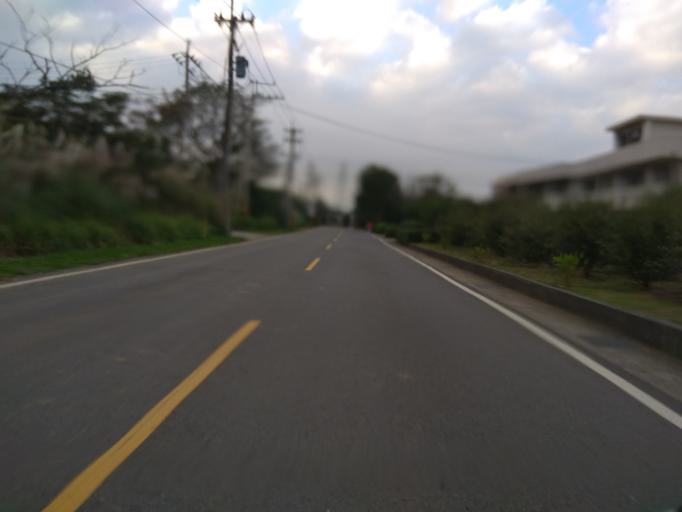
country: TW
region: Taiwan
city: Daxi
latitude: 24.8407
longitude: 121.2052
